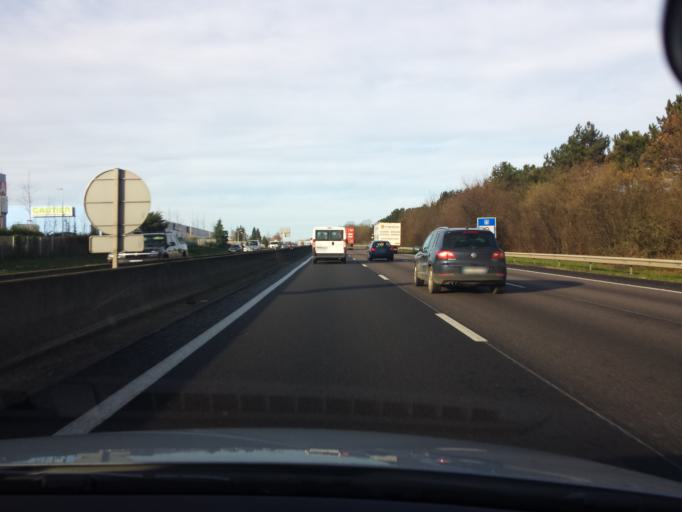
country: FR
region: Ile-de-France
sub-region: Departement des Yvelines
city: Orgeval
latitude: 48.9292
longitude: 1.9868
